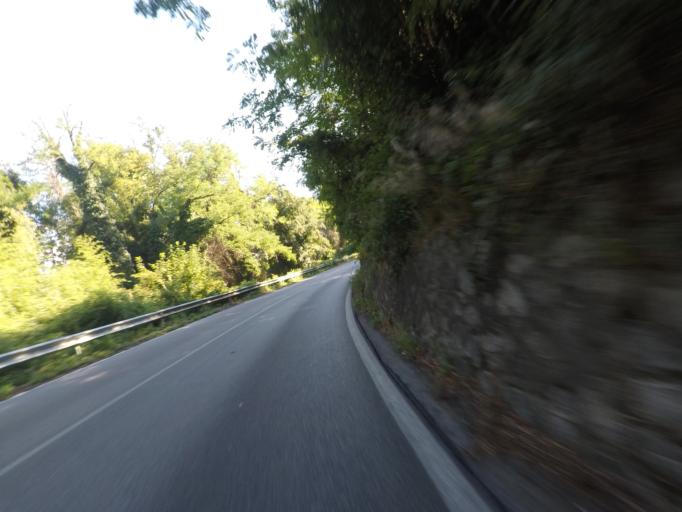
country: IT
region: Tuscany
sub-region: Provincia di Lucca
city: Lucca
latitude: 43.8718
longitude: 10.5205
